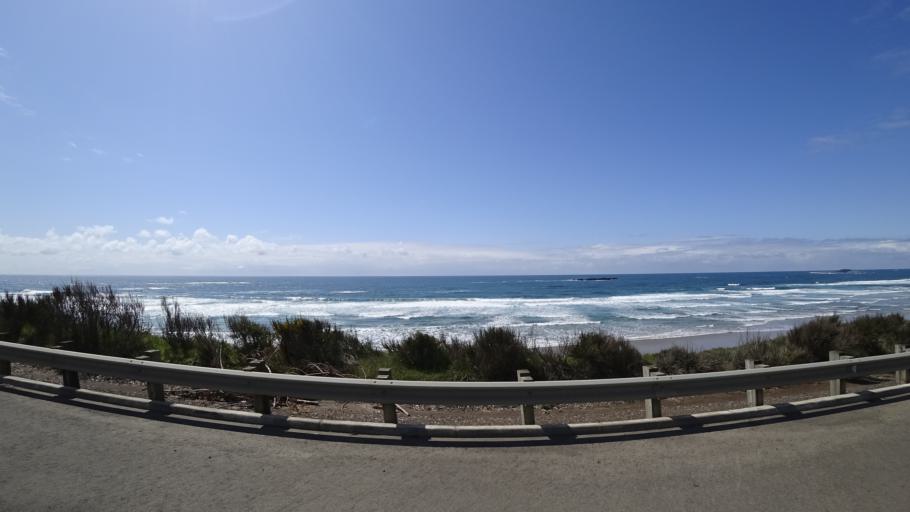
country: US
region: Oregon
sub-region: Lincoln County
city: Depoe Bay
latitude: 44.7276
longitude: -124.0576
